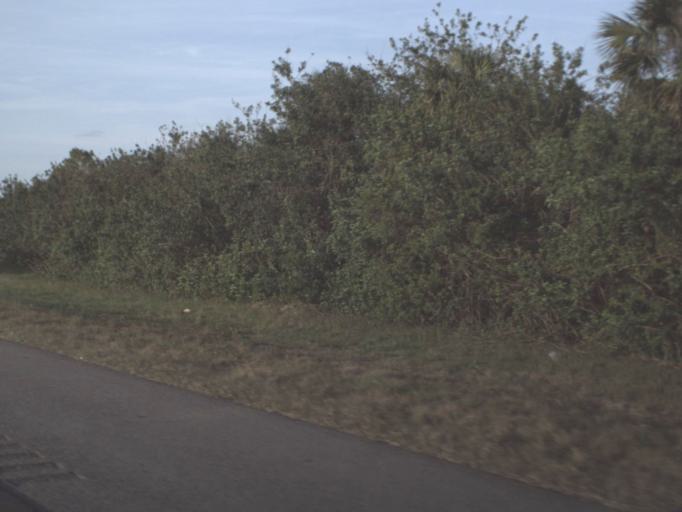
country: US
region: Florida
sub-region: Brevard County
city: Port Saint John
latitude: 28.5336
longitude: -80.8515
